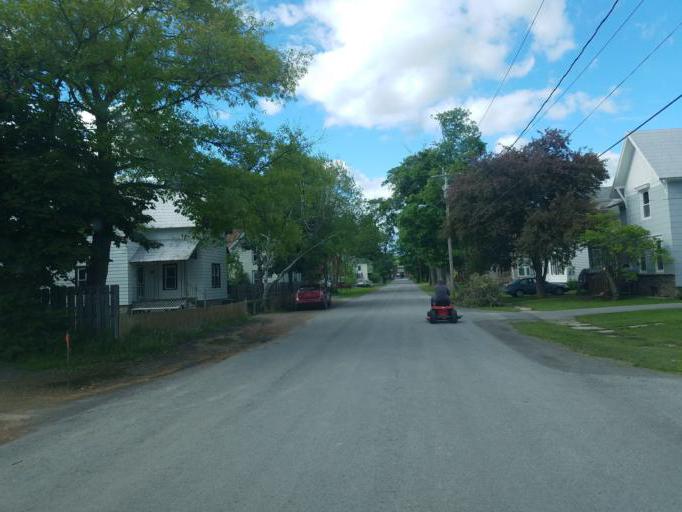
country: US
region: New York
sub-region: Otsego County
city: Richfield Springs
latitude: 42.8509
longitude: -74.9885
